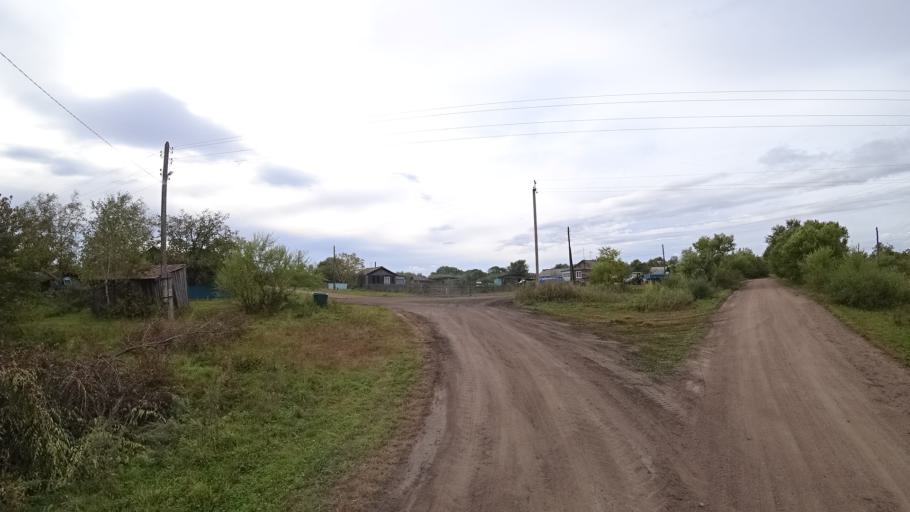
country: RU
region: Amur
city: Arkhara
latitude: 49.3515
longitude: 130.1111
